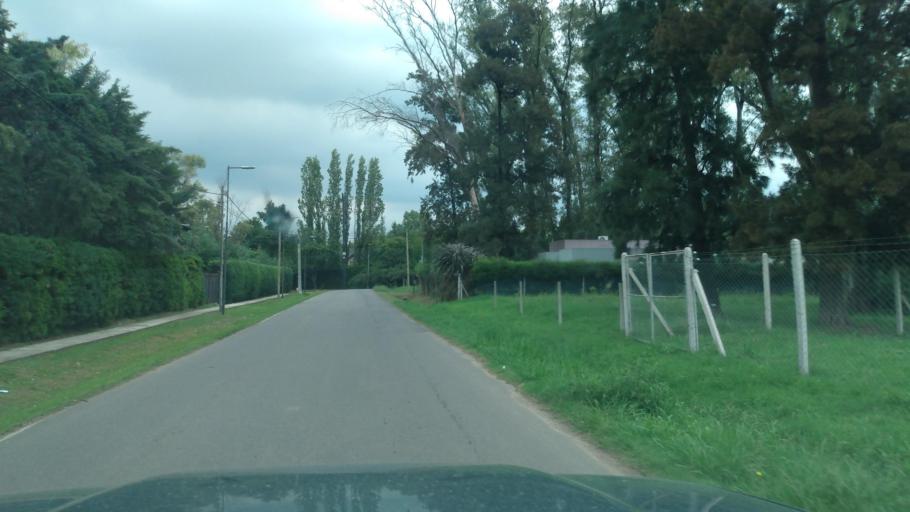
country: AR
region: Buenos Aires
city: Hurlingham
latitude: -34.5759
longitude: -58.7009
